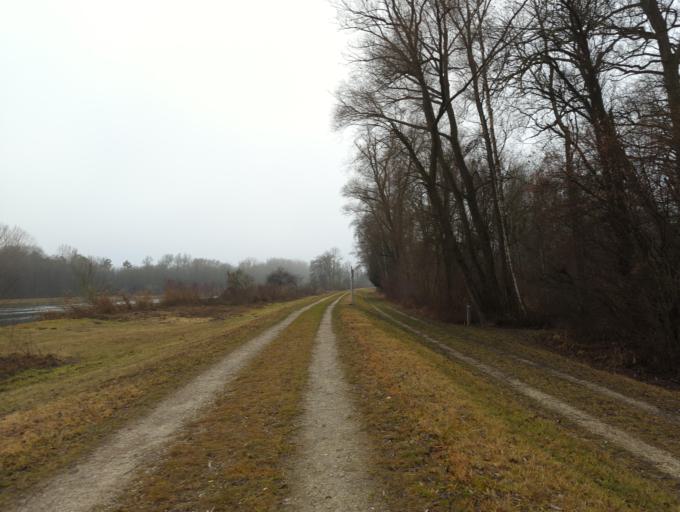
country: DE
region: Bavaria
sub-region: Swabia
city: Offingen
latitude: 48.4955
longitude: 10.3749
